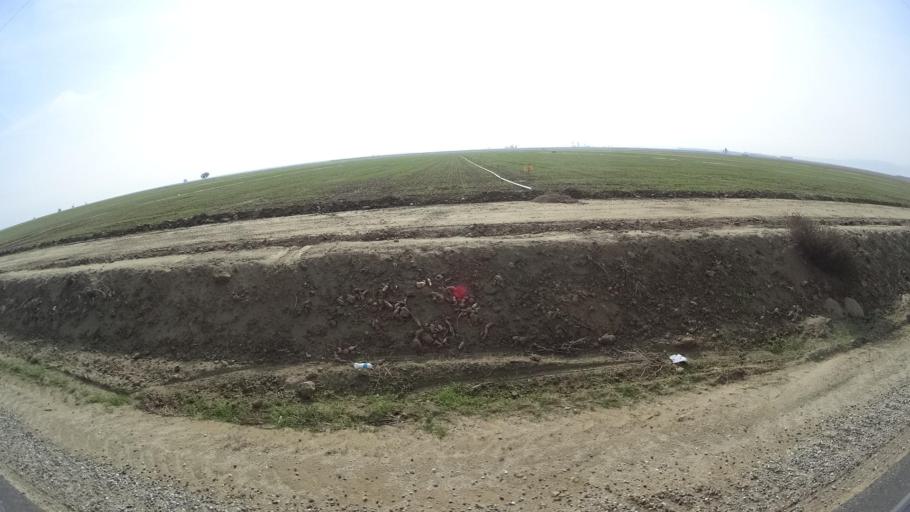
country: US
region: California
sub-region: Kern County
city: Arvin
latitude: 35.0454
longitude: -118.9025
